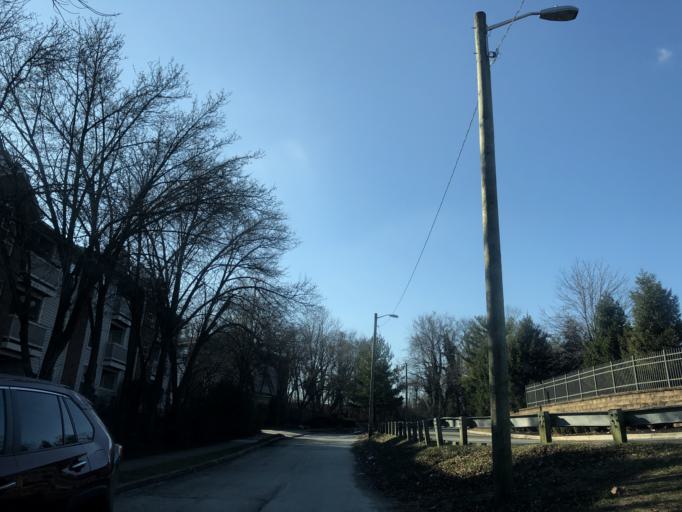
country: US
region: Pennsylvania
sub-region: Montgomery County
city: Bala-Cynwyd
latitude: 40.0054
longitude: -75.2114
